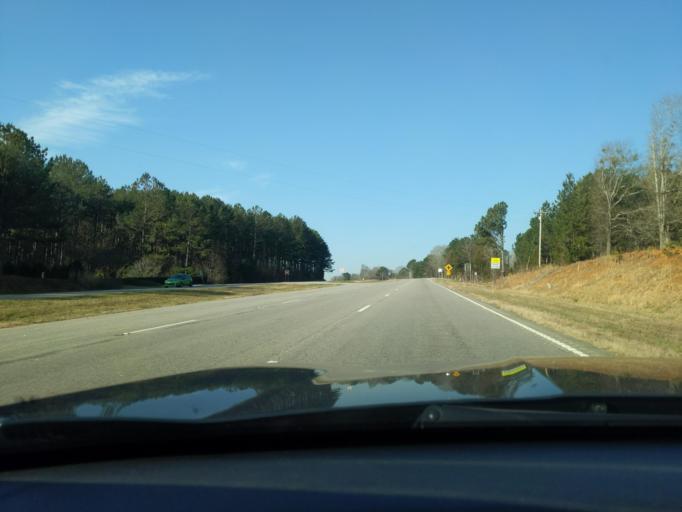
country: US
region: South Carolina
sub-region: Greenwood County
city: Greenwood
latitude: 34.1893
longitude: -82.2691
